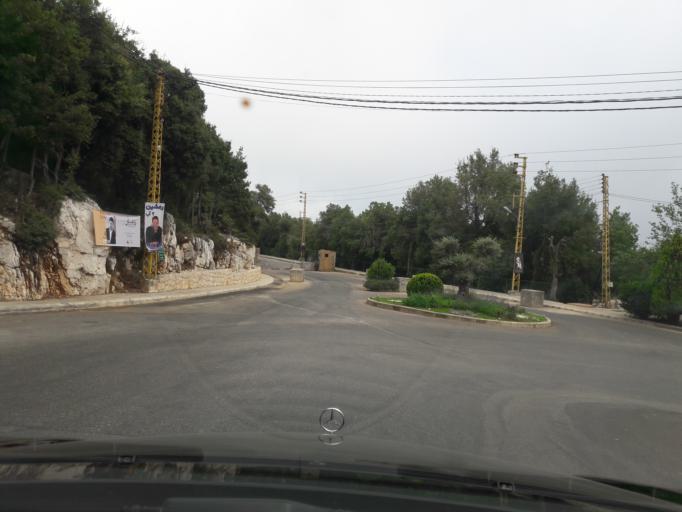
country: LB
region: Mont-Liban
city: Djounie
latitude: 33.9876
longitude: 35.6829
